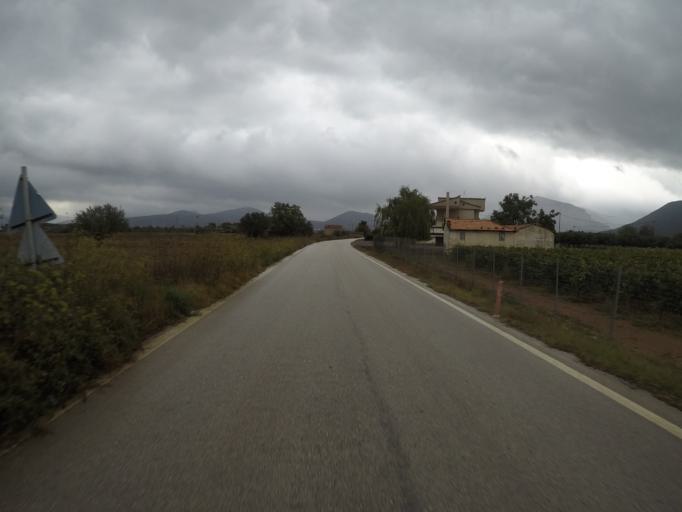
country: GR
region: Peloponnese
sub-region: Nomos Arkadias
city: Tripoli
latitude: 37.5671
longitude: 22.4076
